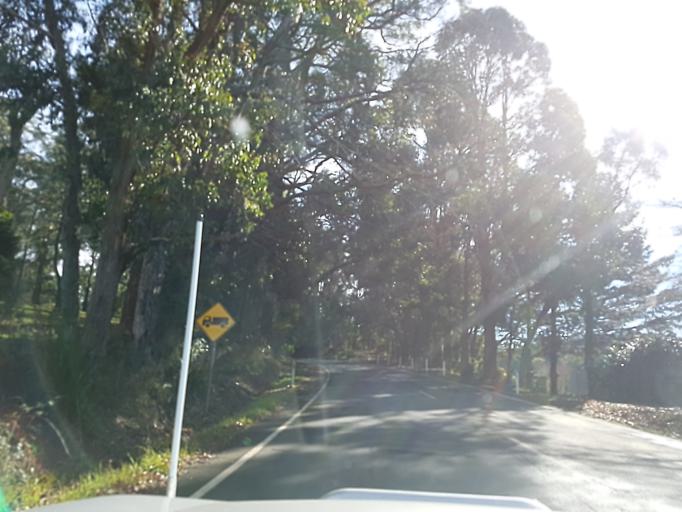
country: AU
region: Victoria
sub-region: Yarra Ranges
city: Healesville
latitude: -37.5444
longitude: 145.4822
